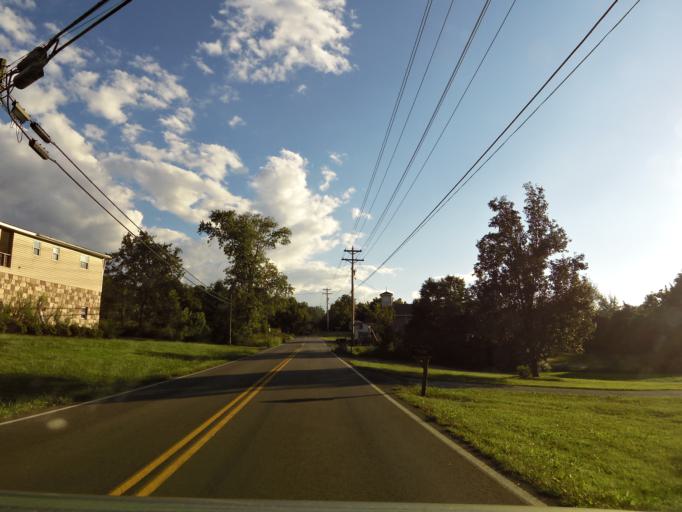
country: US
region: Tennessee
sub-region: Grainger County
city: Rutledge
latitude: 36.2755
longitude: -83.5191
